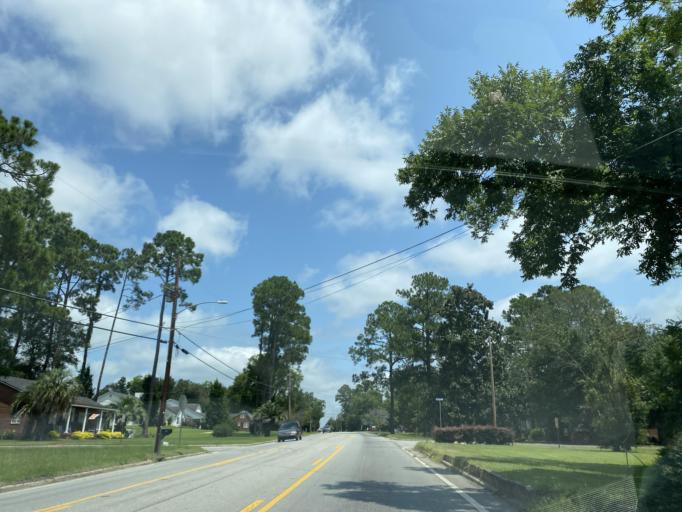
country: US
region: Georgia
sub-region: Telfair County
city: McRae
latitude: 32.0599
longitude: -82.9036
